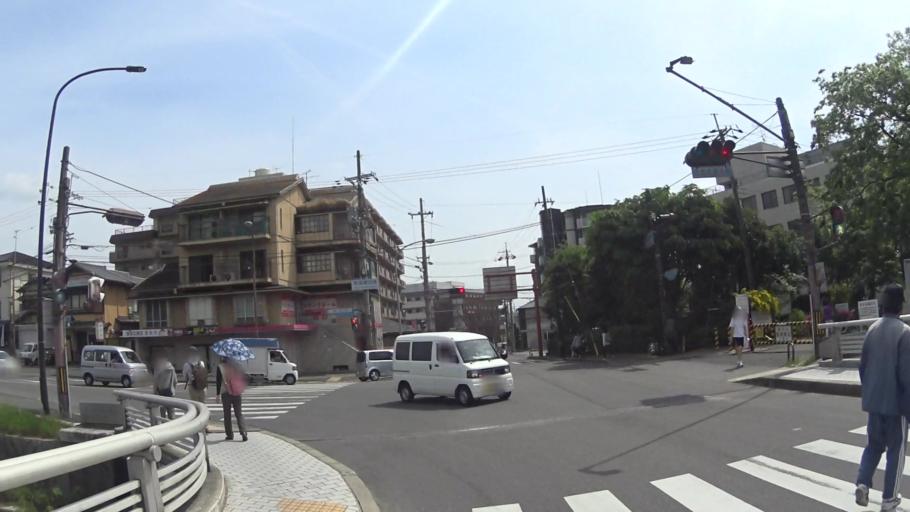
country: JP
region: Kyoto
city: Muko
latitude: 35.0019
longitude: 135.6902
